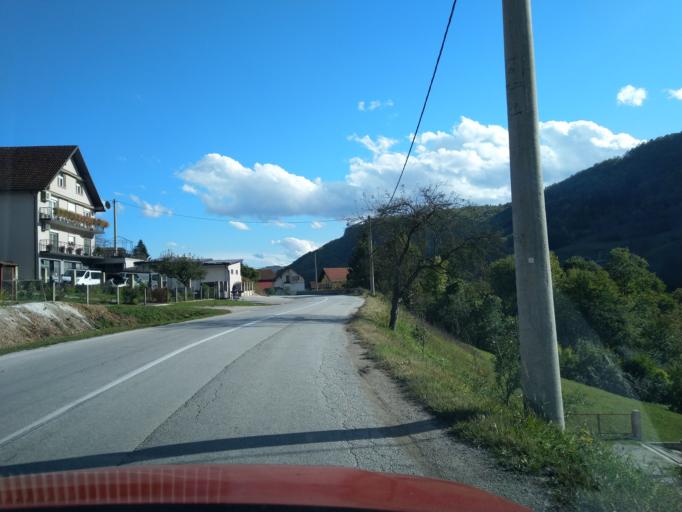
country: RS
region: Central Serbia
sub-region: Zlatiborski Okrug
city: Uzice
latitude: 43.8714
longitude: 19.7955
